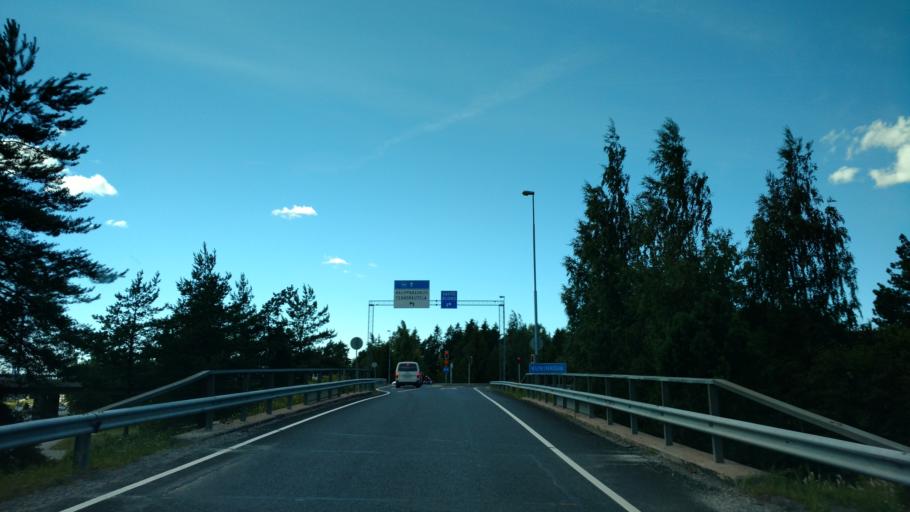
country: FI
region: Varsinais-Suomi
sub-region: Turku
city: Rusko
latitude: 60.4972
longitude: 22.2329
